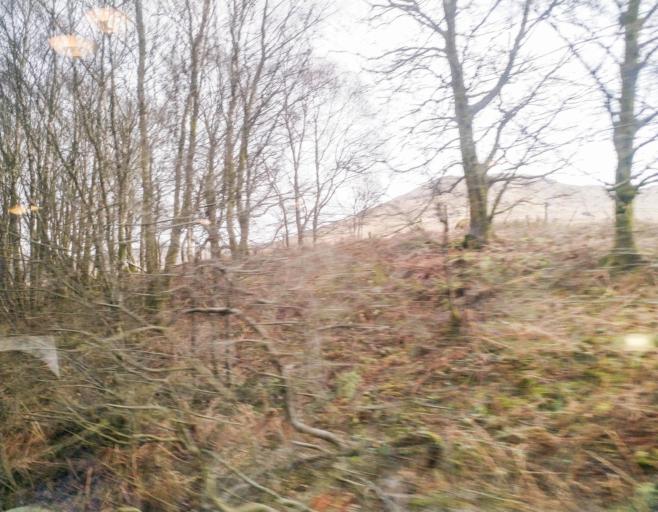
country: GB
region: Scotland
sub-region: Argyll and Bute
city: Garelochhead
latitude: 56.3680
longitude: -4.6601
